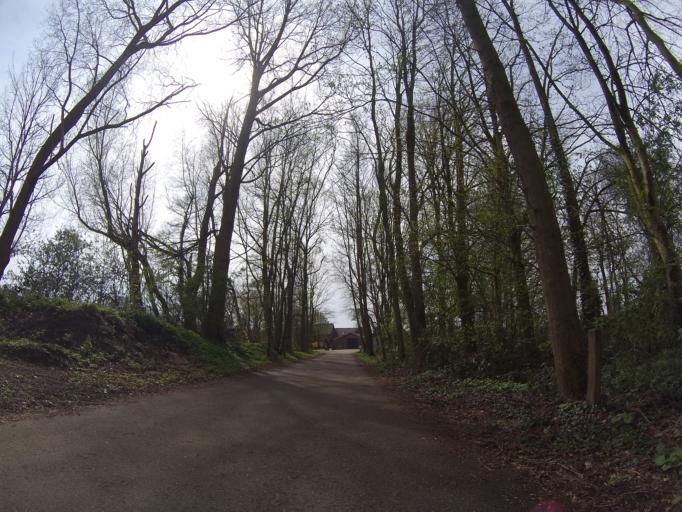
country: NL
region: Gelderland
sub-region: Gemeente Barneveld
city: Barneveld
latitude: 52.1563
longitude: 5.5934
